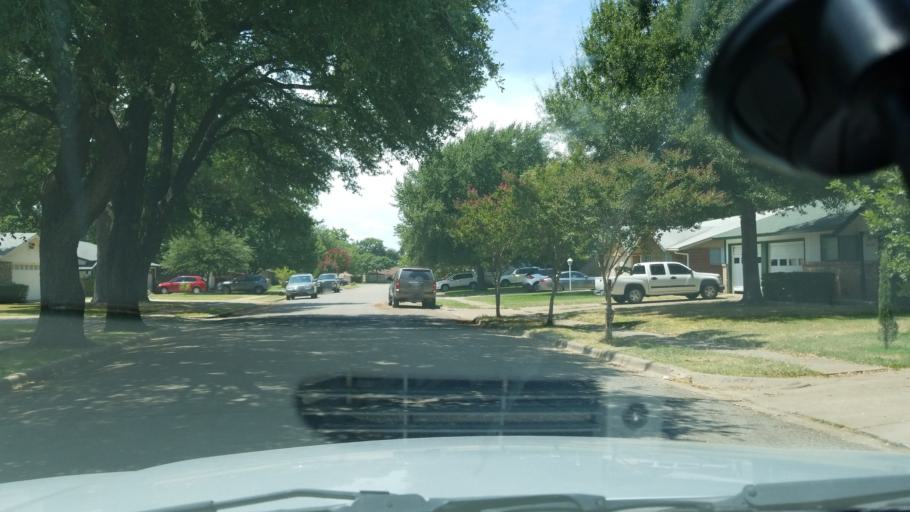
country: US
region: Texas
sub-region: Dallas County
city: Irving
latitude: 32.8255
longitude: -96.9881
